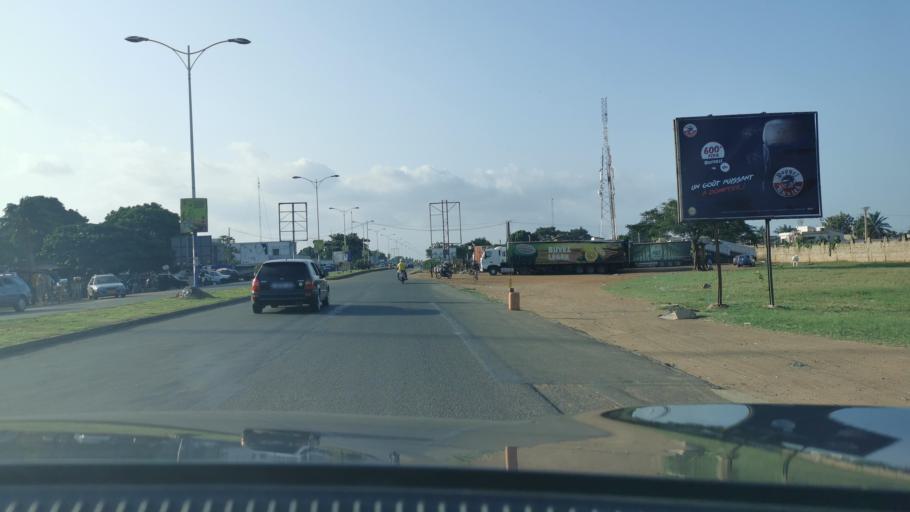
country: TG
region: Maritime
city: Lome
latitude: 6.2140
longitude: 1.2088
